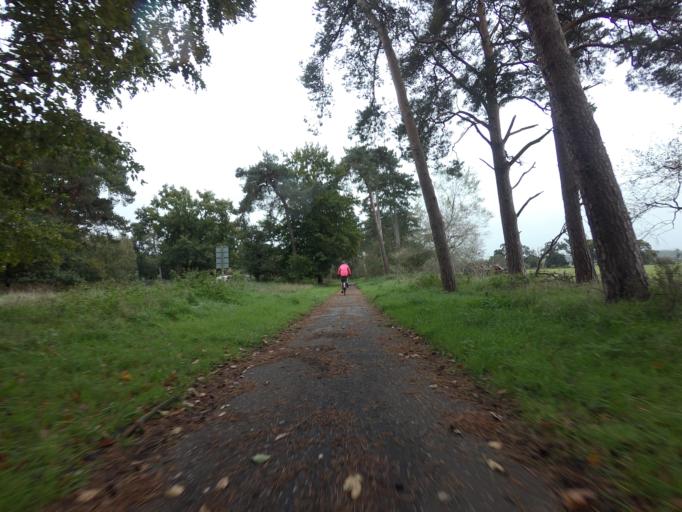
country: GB
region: England
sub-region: Norfolk
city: Dersingham
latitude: 52.8108
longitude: 0.4839
